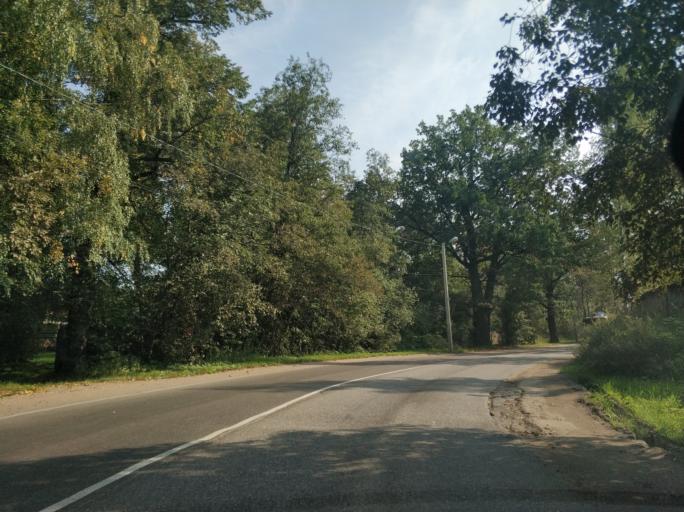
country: RU
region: Leningrad
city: Yanino Vtoroye
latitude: 60.0129
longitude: 30.5908
